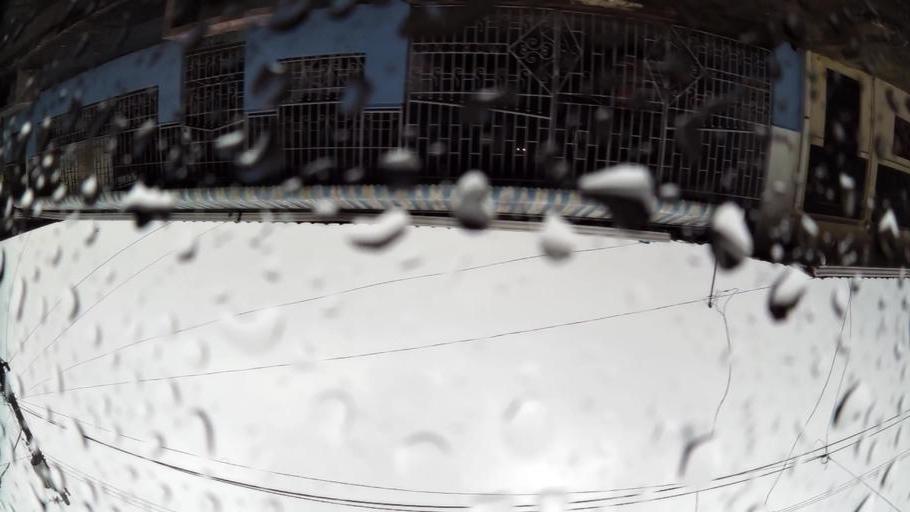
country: PA
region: Colon
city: Puerto Pilon
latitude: 9.3574
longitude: -79.7922
